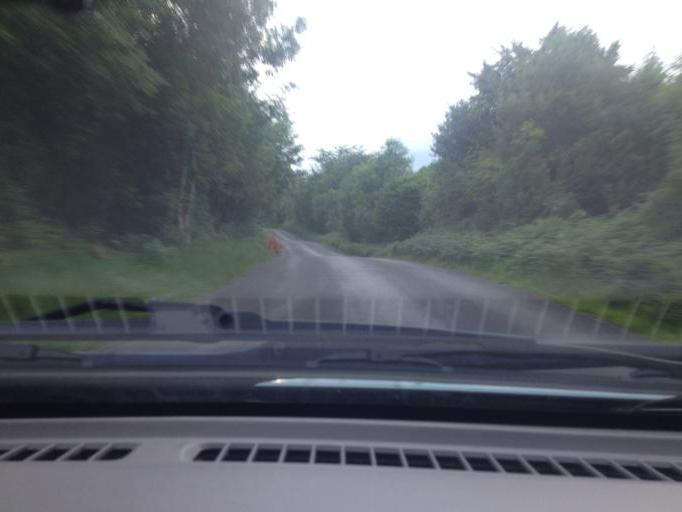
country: IE
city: Ballisodare
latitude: 54.2152
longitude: -8.4763
